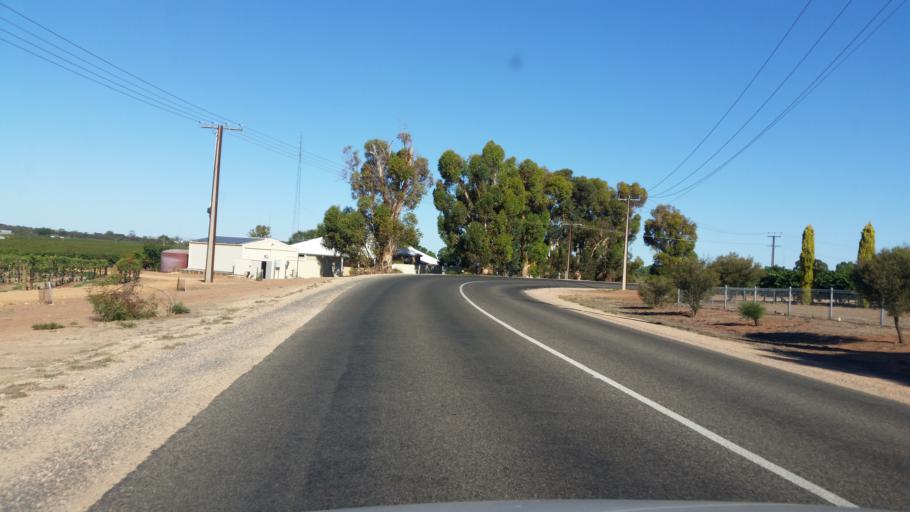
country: AU
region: South Australia
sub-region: Loxton Waikerie
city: Waikerie
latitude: -34.1900
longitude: 139.9871
